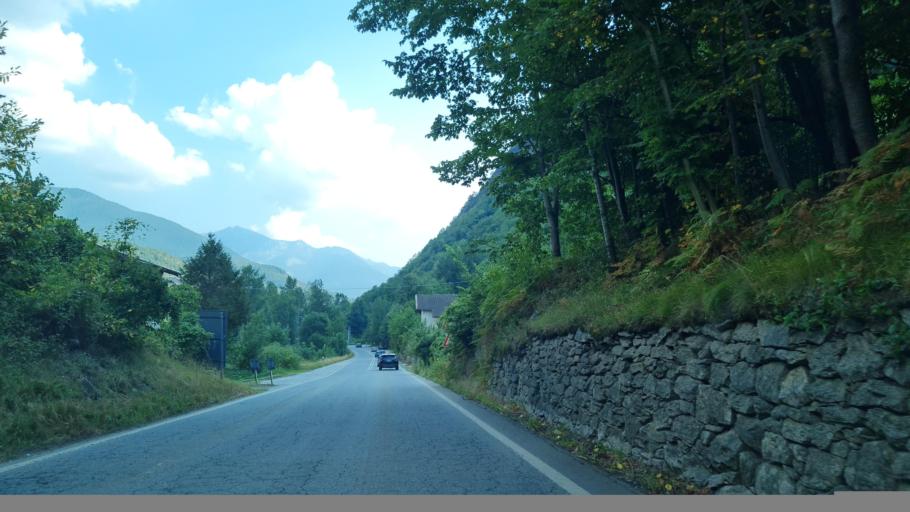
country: IT
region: Piedmont
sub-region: Provincia Verbano-Cusio-Ossola
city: Montecrestese
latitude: 46.1900
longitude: 8.3210
